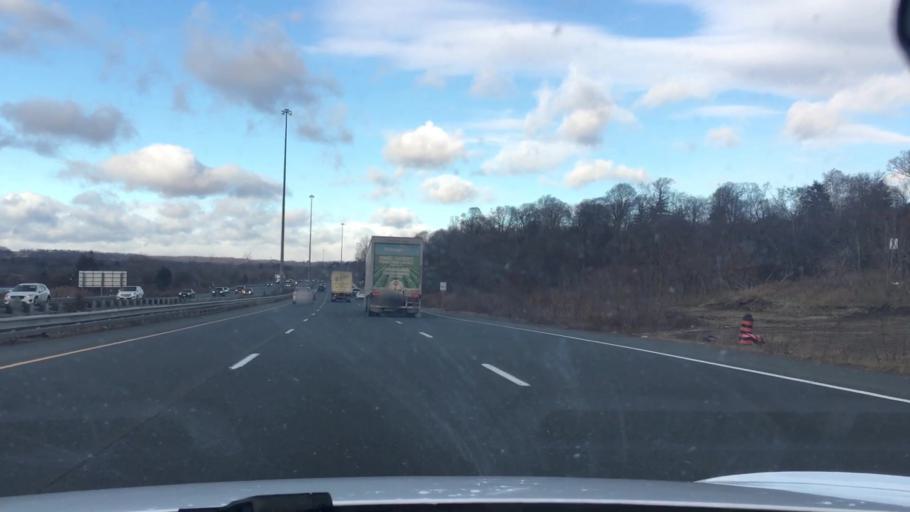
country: CA
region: Ontario
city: Hamilton
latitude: 43.2715
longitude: -79.8919
